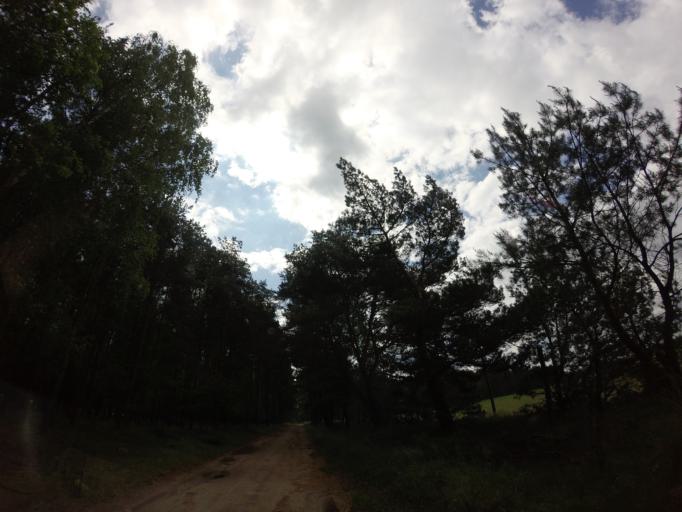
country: PL
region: West Pomeranian Voivodeship
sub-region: Powiat choszczenski
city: Drawno
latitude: 53.1800
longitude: 15.8711
